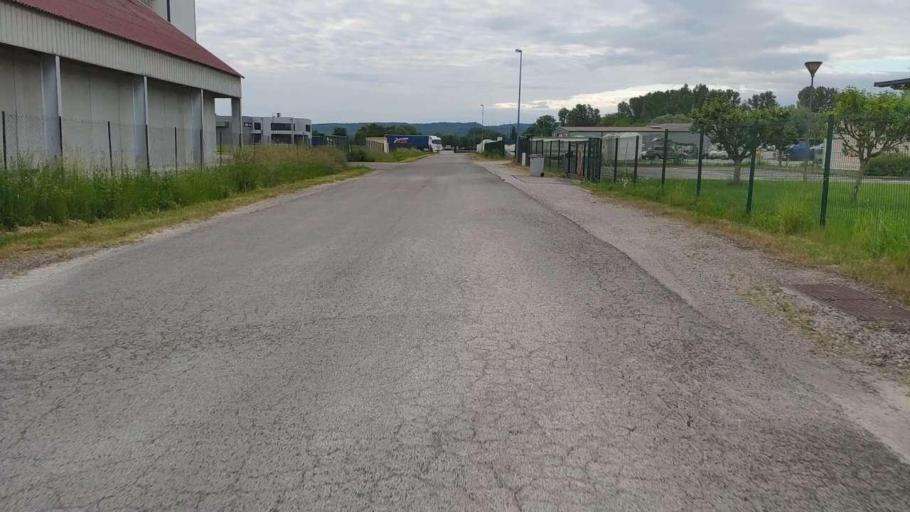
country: FR
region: Franche-Comte
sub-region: Departement du Jura
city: Bletterans
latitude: 46.7489
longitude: 5.4709
